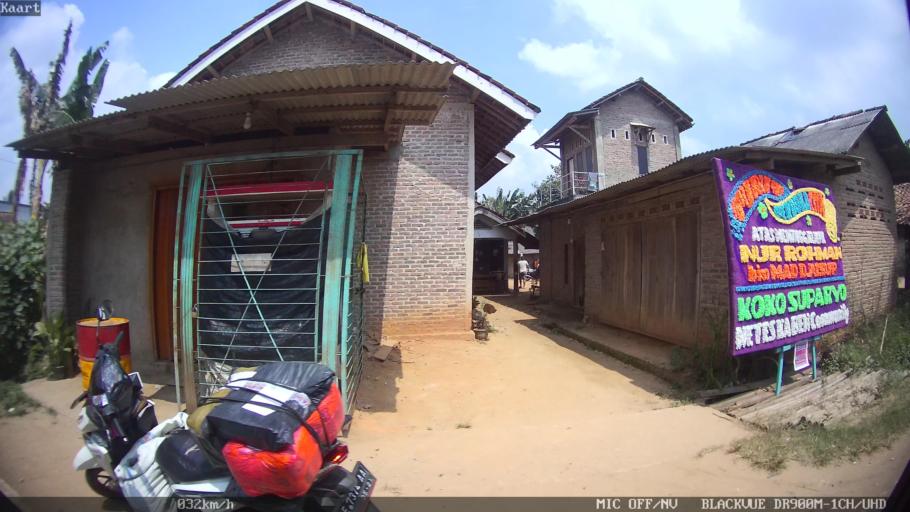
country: ID
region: Lampung
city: Pringsewu
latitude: -5.3859
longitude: 104.9696
